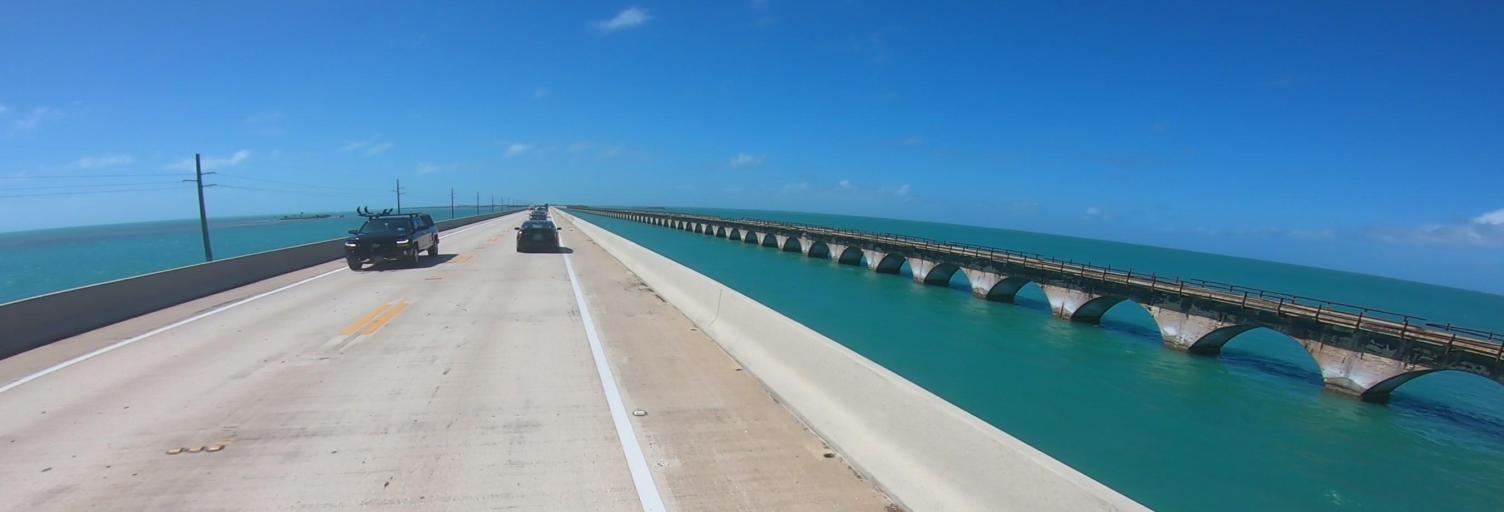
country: US
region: Florida
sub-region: Monroe County
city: Marathon
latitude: 24.6879
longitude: -81.2086
